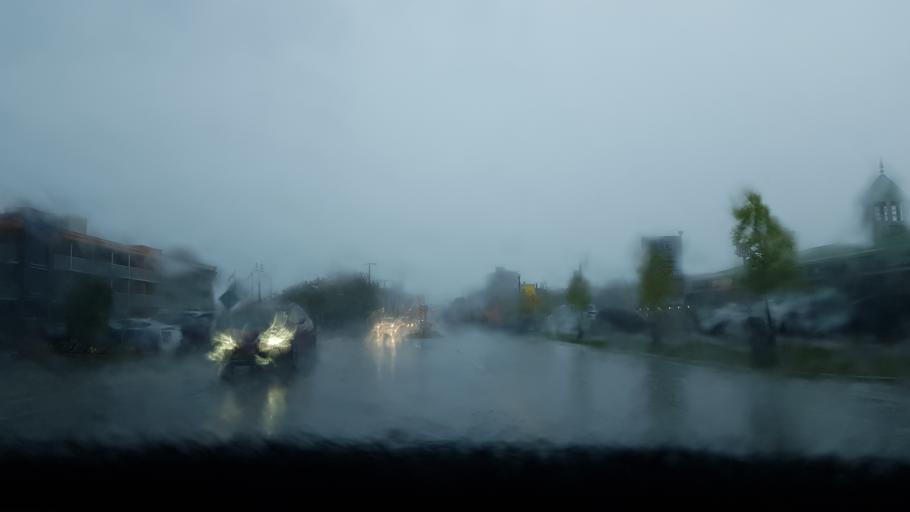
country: CA
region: Ontario
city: Peterborough
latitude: 44.2983
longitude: -78.3196
